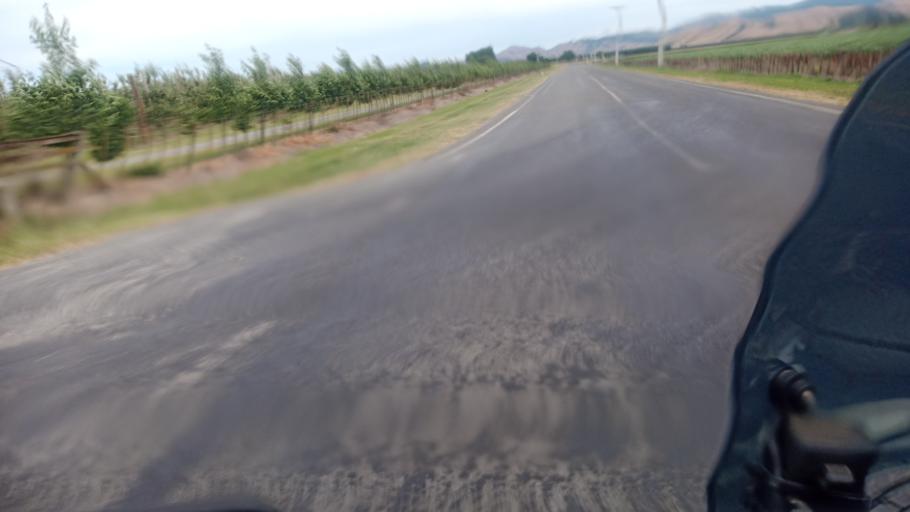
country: NZ
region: Gisborne
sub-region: Gisborne District
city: Gisborne
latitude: -38.6029
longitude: 177.8979
